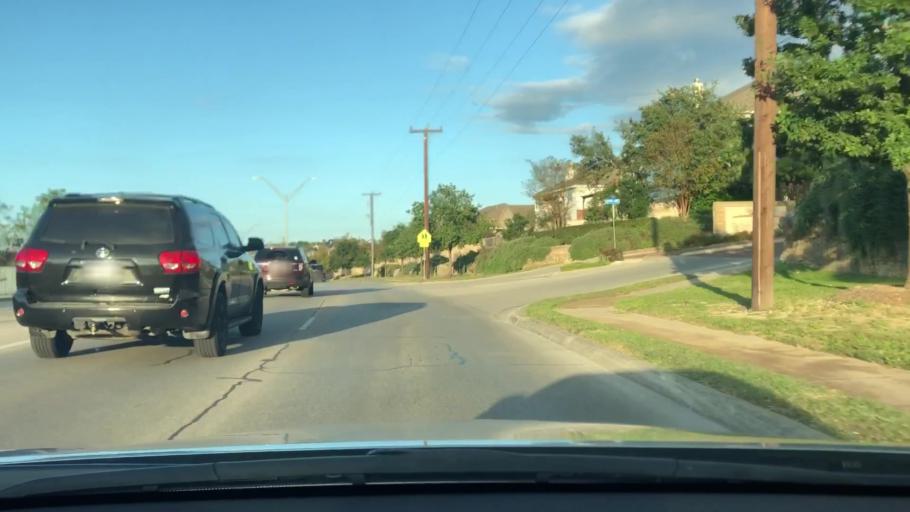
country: US
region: Texas
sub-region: Bexar County
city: Hollywood Park
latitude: 29.6364
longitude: -98.5082
